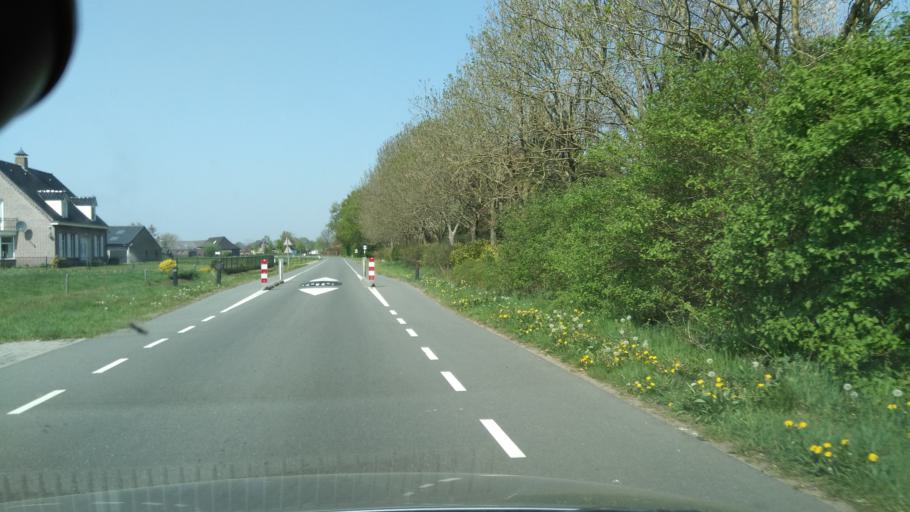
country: NL
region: North Brabant
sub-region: Gemeente Baarle-Nassau
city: Baarle-Nassau
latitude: 51.4896
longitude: 4.8624
